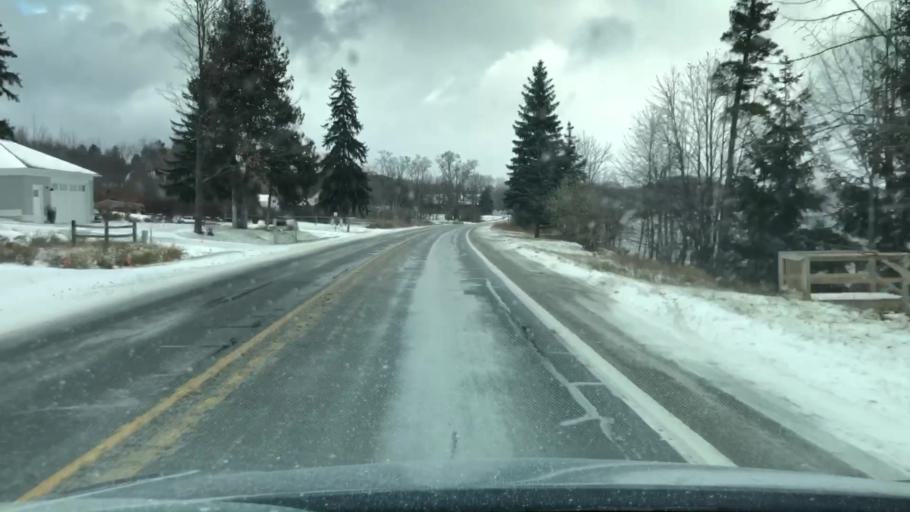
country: US
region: Michigan
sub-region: Grand Traverse County
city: Traverse City
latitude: 44.8155
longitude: -85.5580
